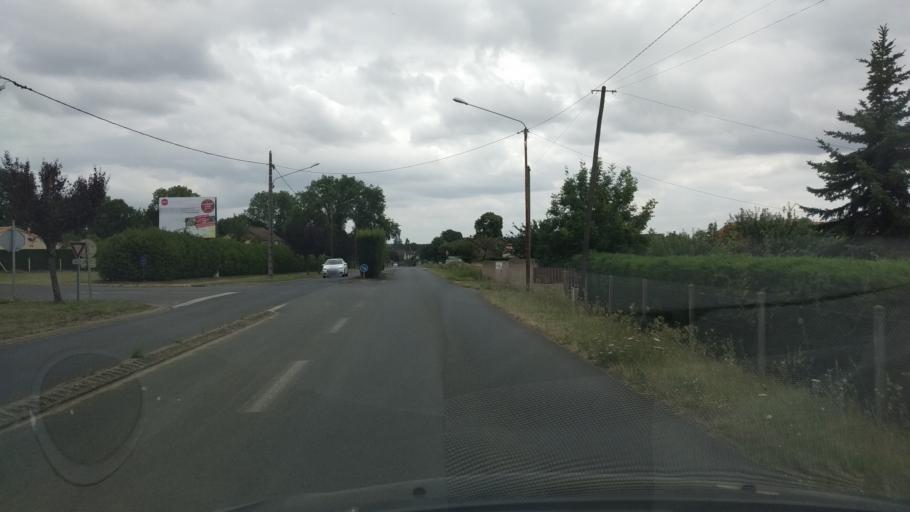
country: FR
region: Poitou-Charentes
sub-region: Departement de la Vienne
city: Roches-Premarie-Andille
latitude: 46.4883
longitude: 0.3685
